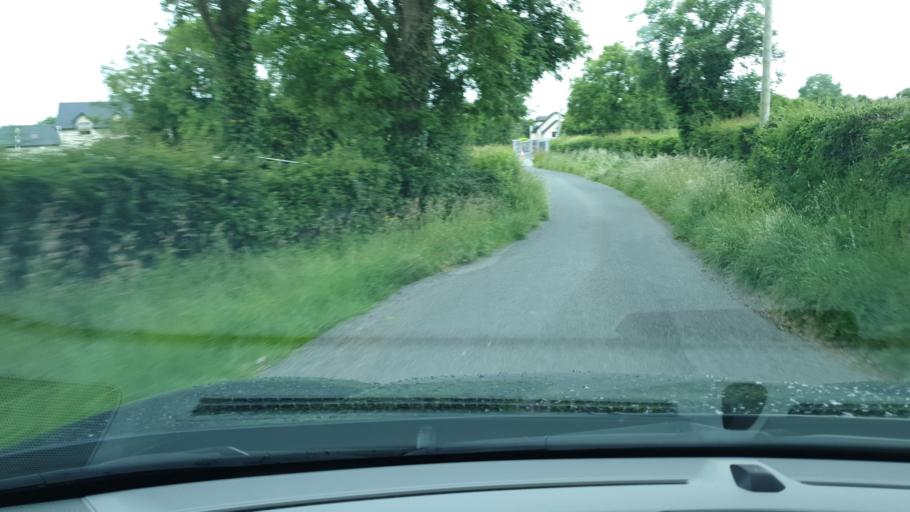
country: IE
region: Leinster
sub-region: An Mhi
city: Ashbourne
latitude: 53.5272
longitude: -6.3907
